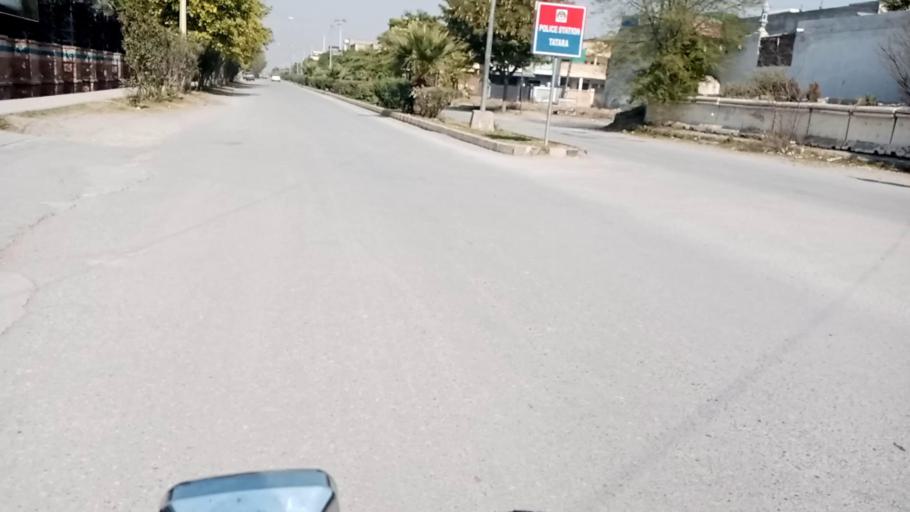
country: PK
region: Khyber Pakhtunkhwa
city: Peshawar
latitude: 33.9579
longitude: 71.4176
